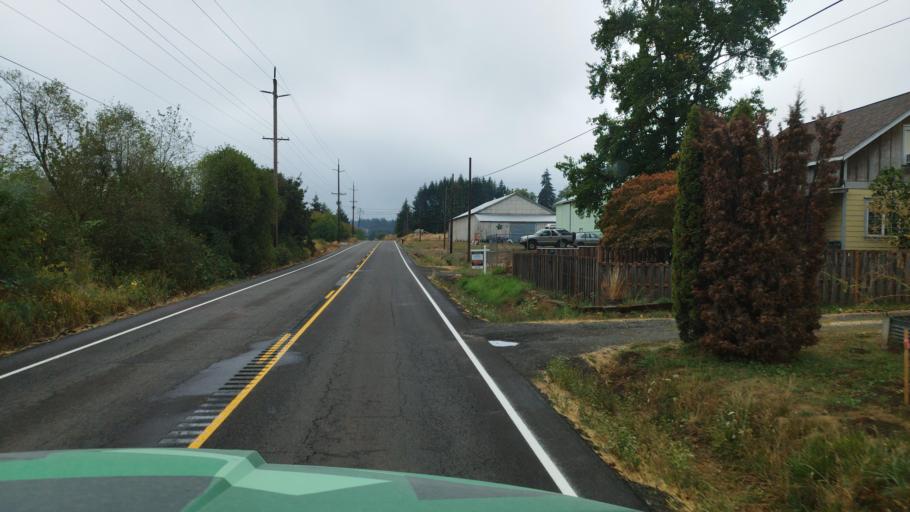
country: US
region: Oregon
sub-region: Yamhill County
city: Yamhill
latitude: 45.4243
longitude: -123.1371
